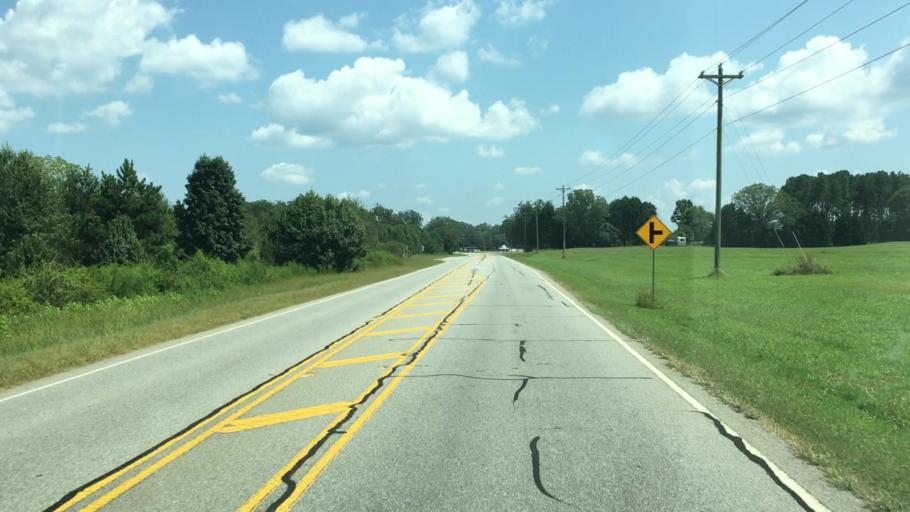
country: US
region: Georgia
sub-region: Oconee County
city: Bogart
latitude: 33.8844
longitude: -83.5545
